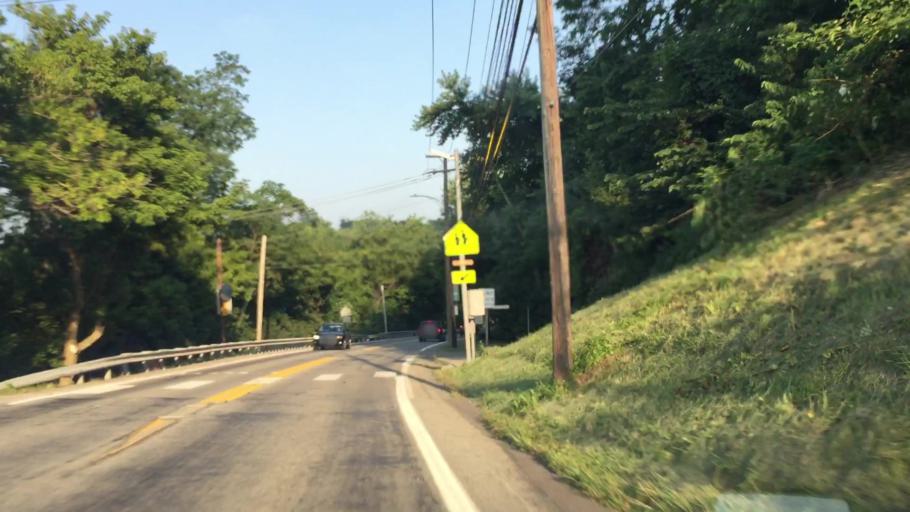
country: US
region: Pennsylvania
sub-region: Allegheny County
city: Bryn Mawr
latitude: 40.3158
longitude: -80.0934
